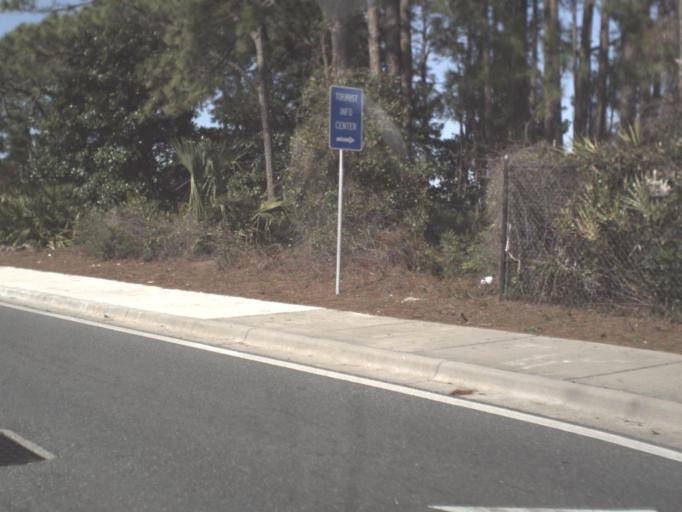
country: US
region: Florida
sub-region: Bay County
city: Panama City Beach
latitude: 30.1880
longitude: -85.8158
